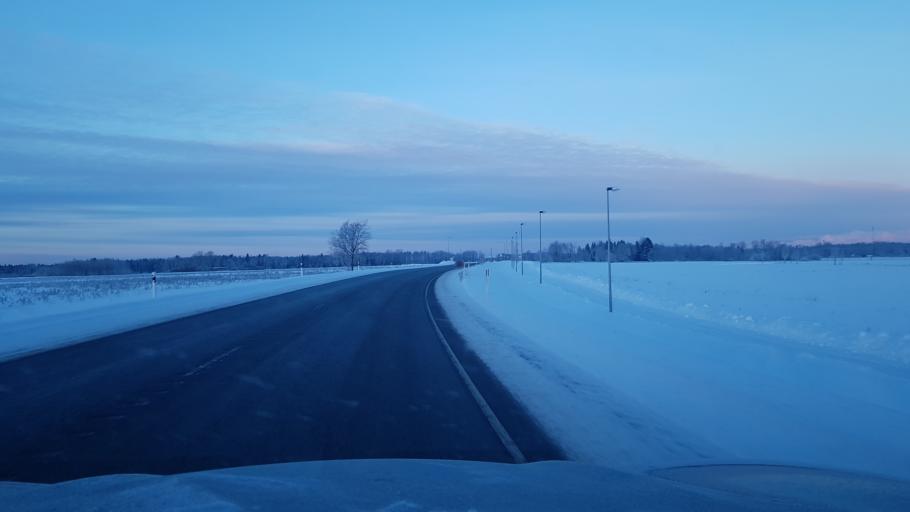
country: EE
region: Ida-Virumaa
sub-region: Narva linn
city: Narva
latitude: 59.3901
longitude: 28.1004
